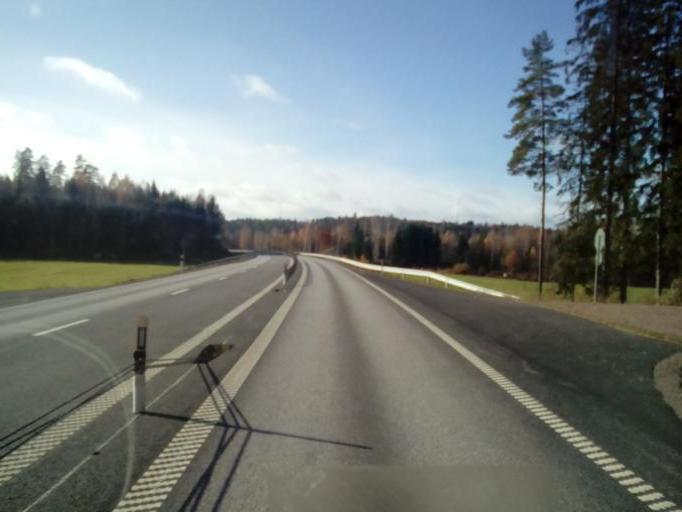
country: SE
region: Kalmar
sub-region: Vimmerby Kommun
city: Vimmerby
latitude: 57.7050
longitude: 16.0223
